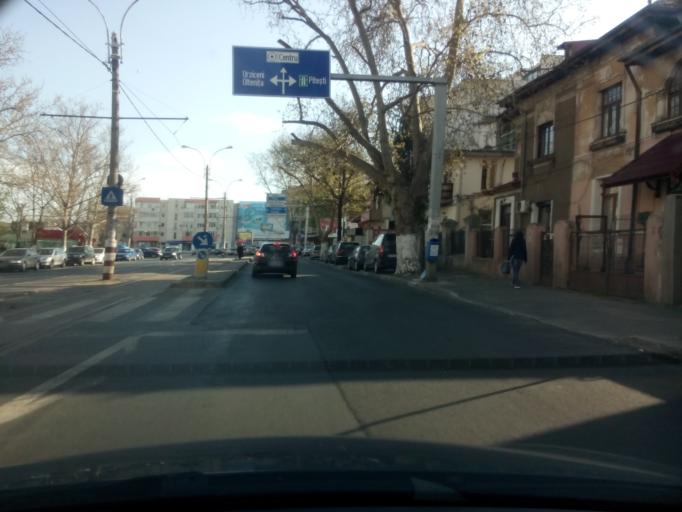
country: RO
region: Bucuresti
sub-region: Municipiul Bucuresti
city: Bucharest
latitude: 44.4545
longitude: 26.1050
